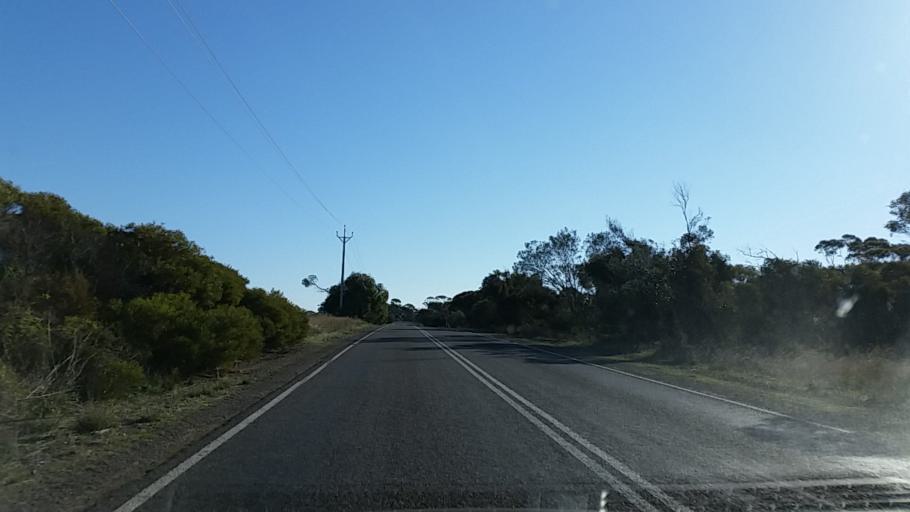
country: AU
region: South Australia
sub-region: Murray Bridge
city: Murray Bridge
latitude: -35.1190
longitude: 139.1622
